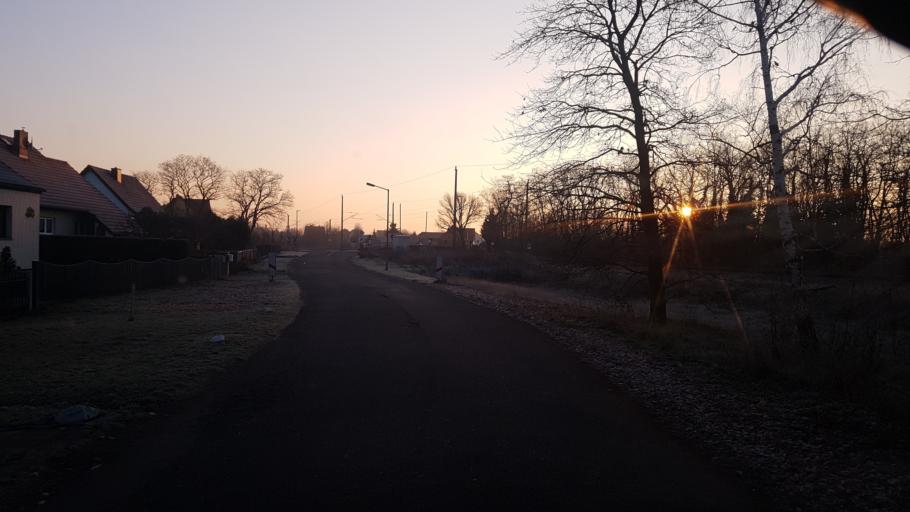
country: DE
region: Brandenburg
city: Tettau
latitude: 51.4752
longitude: 13.7254
